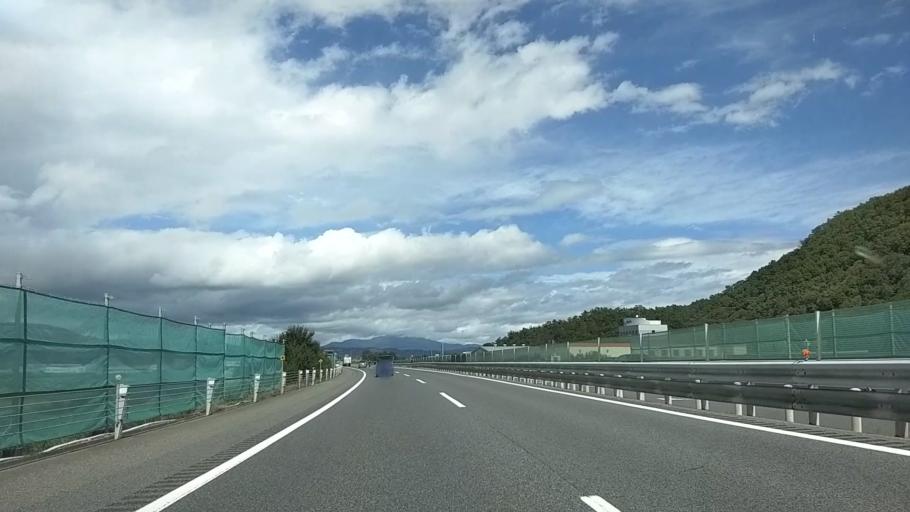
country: JP
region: Nagano
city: Suzaka
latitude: 36.6255
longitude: 138.2736
